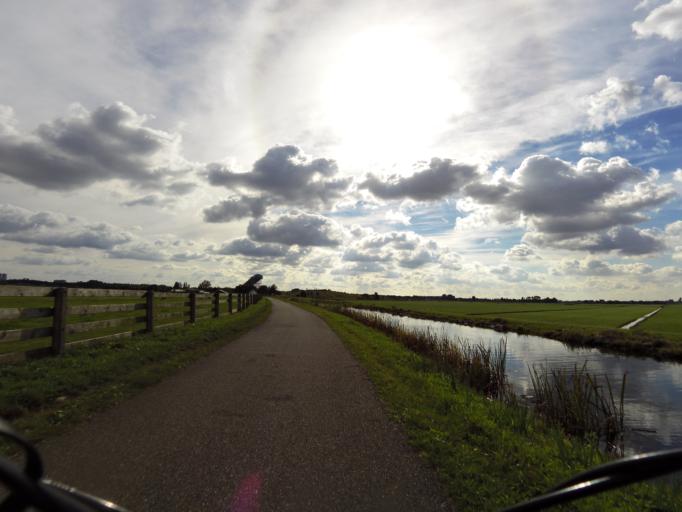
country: NL
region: South Holland
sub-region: Gemeente Zoetermeer
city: Zoetermeer
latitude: 52.0825
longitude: 4.4552
